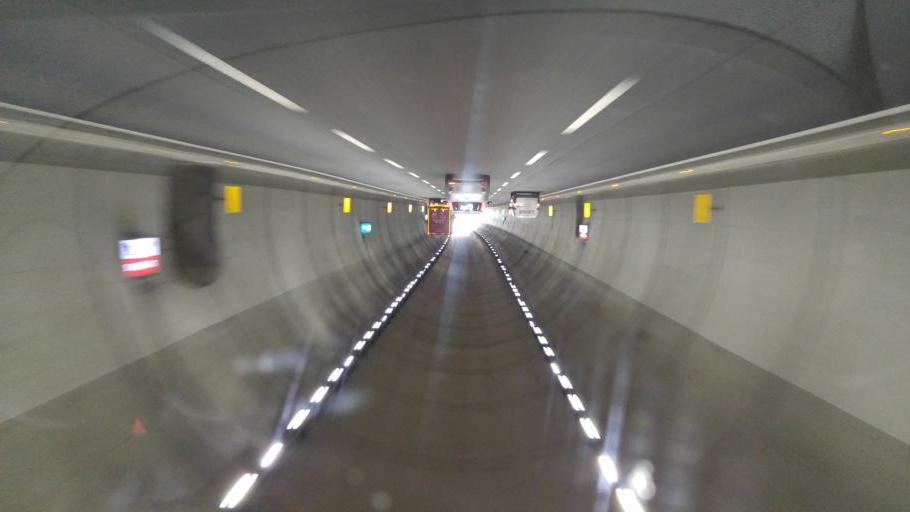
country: IT
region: Emilia-Romagna
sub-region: Provincia di Rimini
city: Riccione
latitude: 43.9793
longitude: 12.6555
